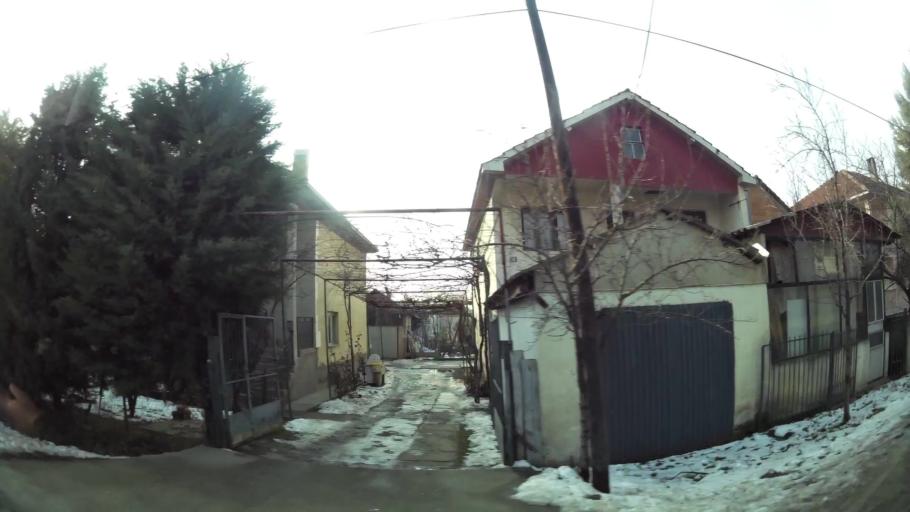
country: MK
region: Ilinden
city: Marino
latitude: 41.9886
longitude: 21.5919
